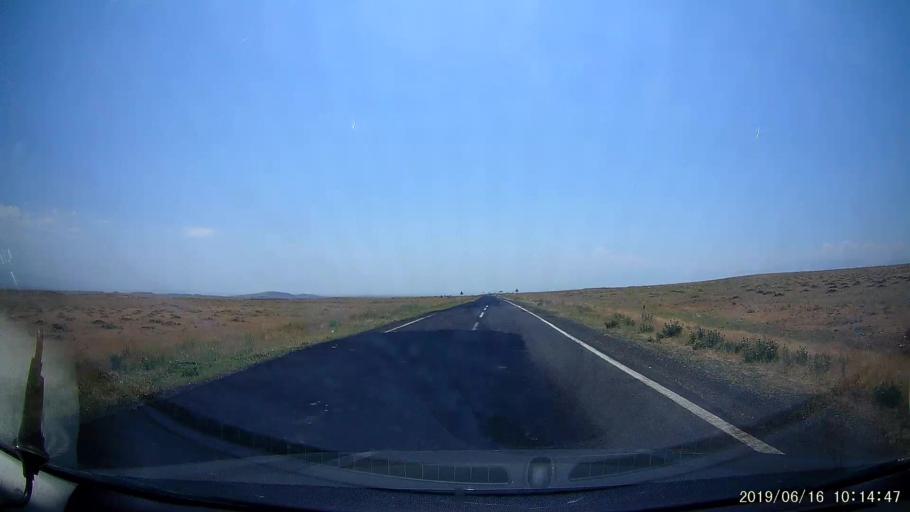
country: TR
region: Igdir
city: Tuzluca
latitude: 40.1818
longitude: 43.6698
